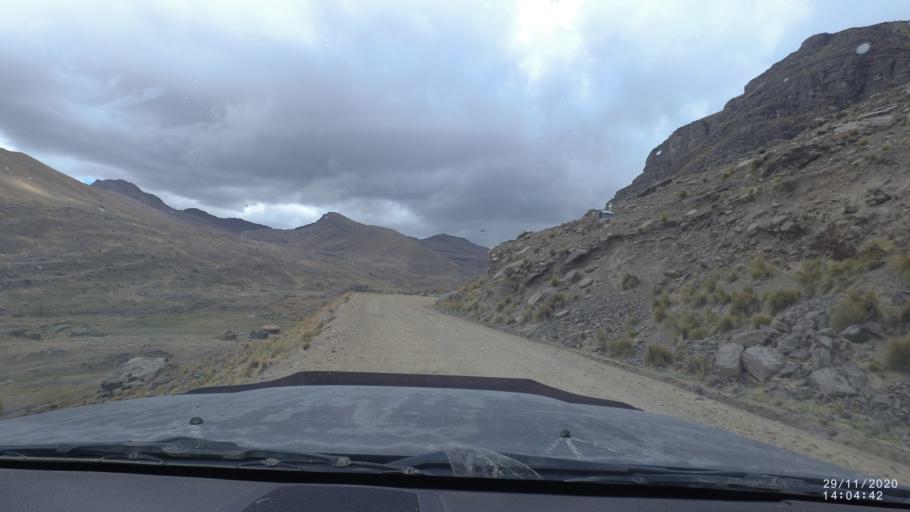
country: BO
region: Cochabamba
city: Sipe Sipe
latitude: -17.2026
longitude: -66.3773
